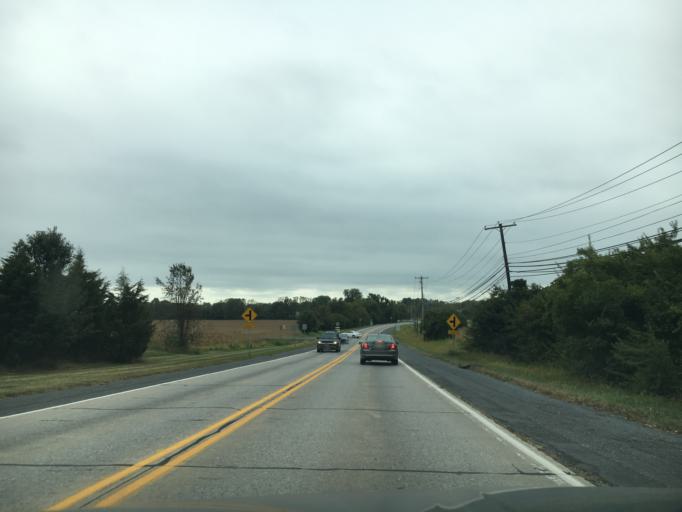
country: US
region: Pennsylvania
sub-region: Northampton County
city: Bath
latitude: 40.6968
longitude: -75.4165
